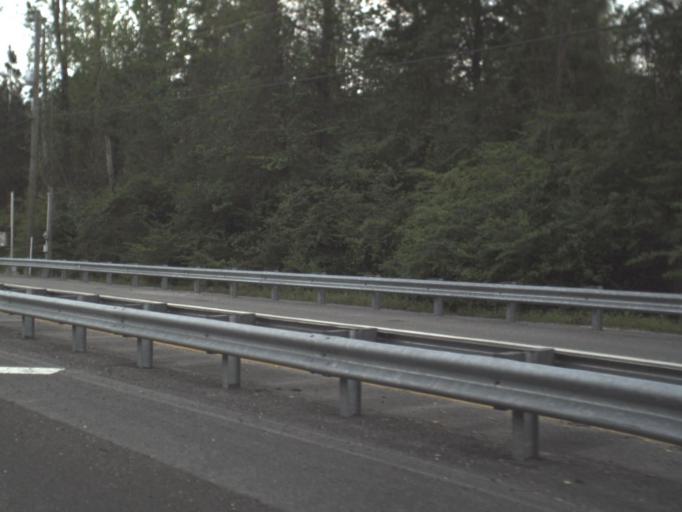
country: US
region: Florida
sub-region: Escambia County
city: Cantonment
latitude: 30.6388
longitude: -87.3414
